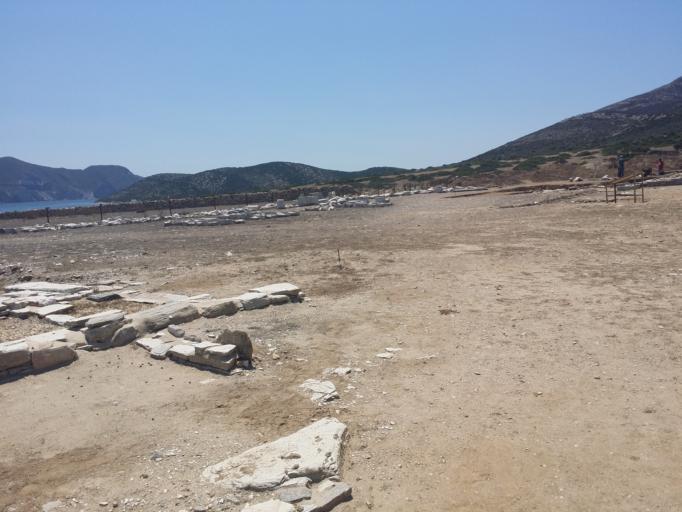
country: GR
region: South Aegean
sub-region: Nomos Kykladon
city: Antiparos
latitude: 36.9707
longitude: 25.0144
